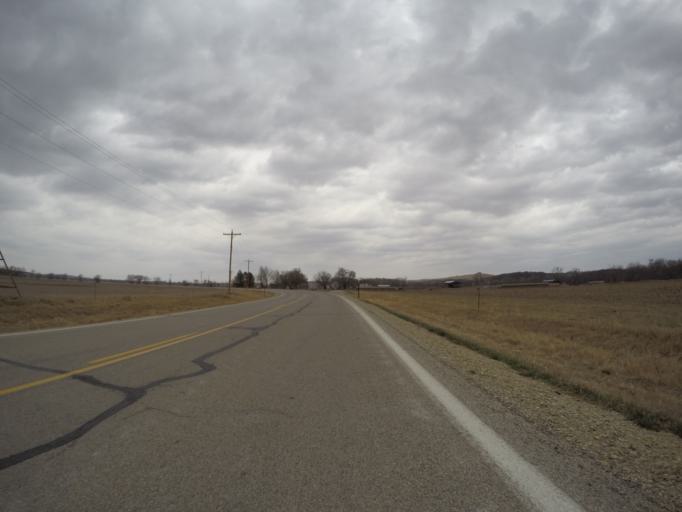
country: US
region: Kansas
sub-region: Riley County
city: Manhattan
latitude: 39.2240
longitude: -96.5577
